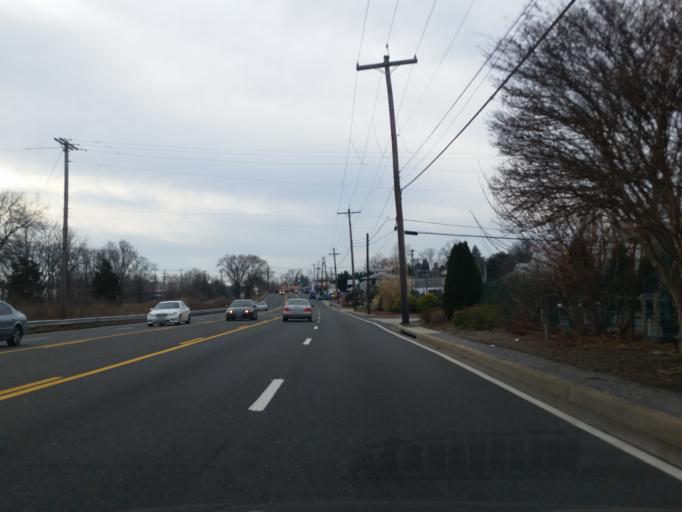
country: US
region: Maryland
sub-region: Prince George's County
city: Beltsville
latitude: 39.0397
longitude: -76.9050
